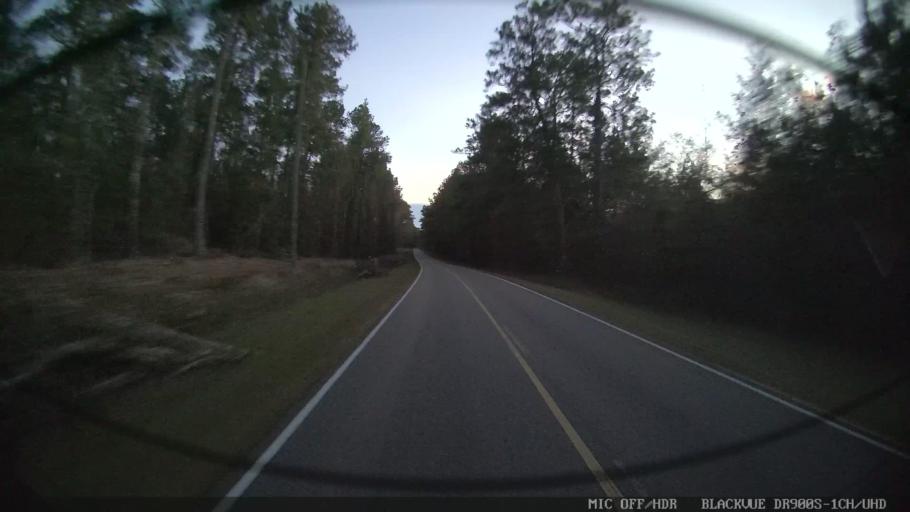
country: US
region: Mississippi
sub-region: Perry County
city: New Augusta
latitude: 31.1277
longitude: -89.1964
